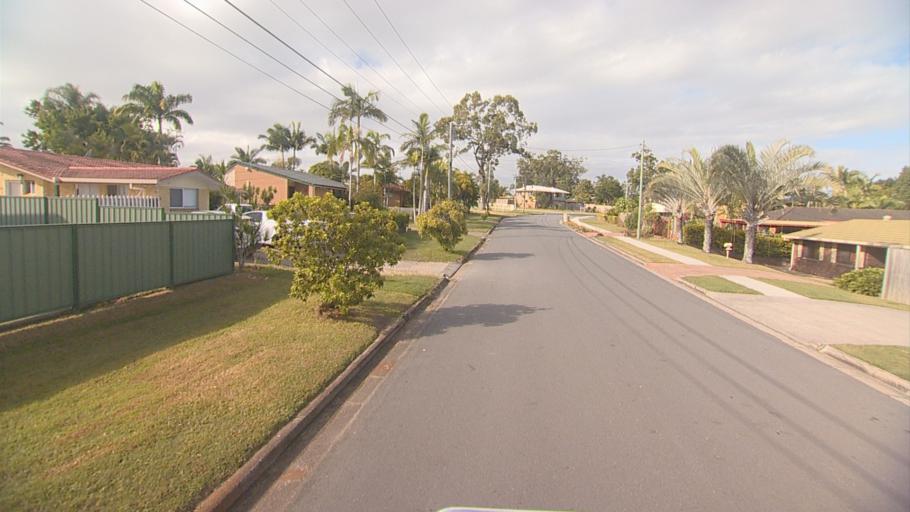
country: AU
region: Queensland
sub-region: Brisbane
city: Sunnybank Hills
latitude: -27.6582
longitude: 153.0470
